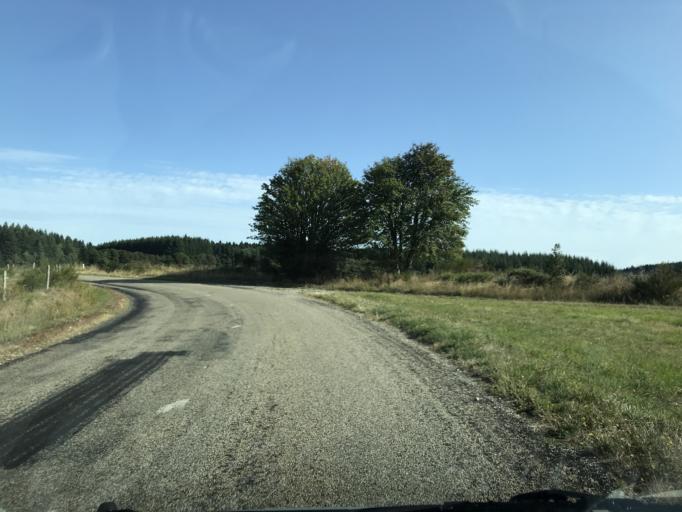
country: FR
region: Rhone-Alpes
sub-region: Departement de l'Ardeche
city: Saint-Agreve
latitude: 45.0268
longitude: 4.4241
